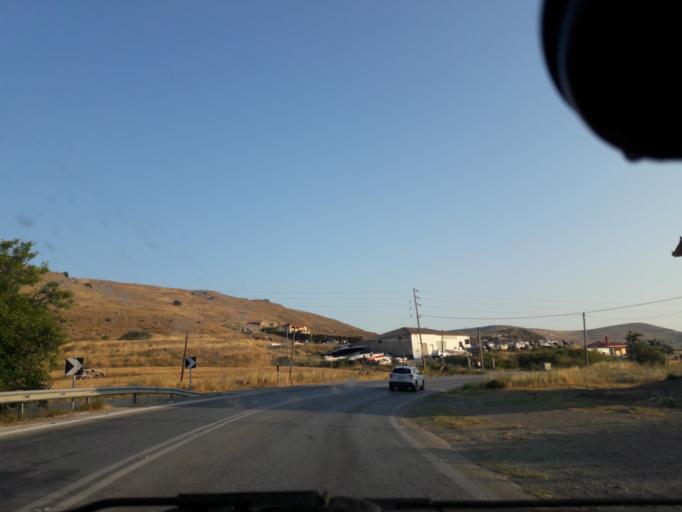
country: GR
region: North Aegean
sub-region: Nomos Lesvou
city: Myrina
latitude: 39.9058
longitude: 25.1122
